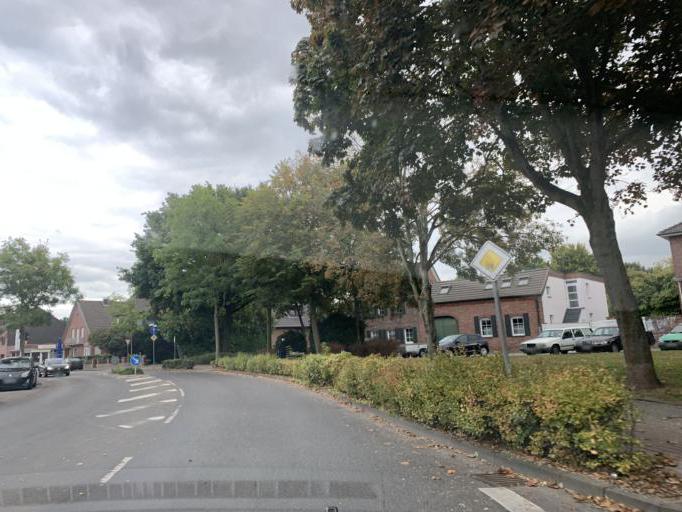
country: DE
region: North Rhine-Westphalia
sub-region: Regierungsbezirk Koln
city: Wassenberg
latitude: 51.0598
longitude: 6.1473
